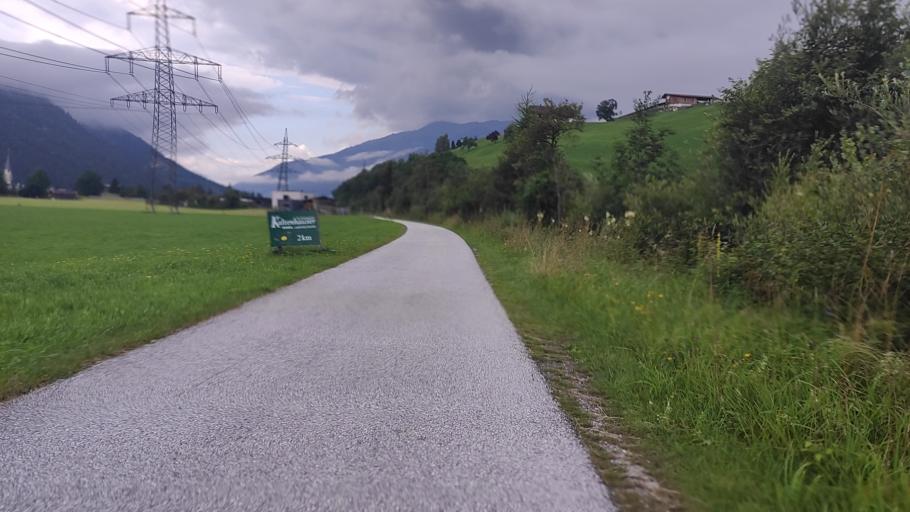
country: AT
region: Salzburg
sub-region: Politischer Bezirk Zell am See
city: Hollersbach im Pinzgau
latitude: 47.2787
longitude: 12.4286
